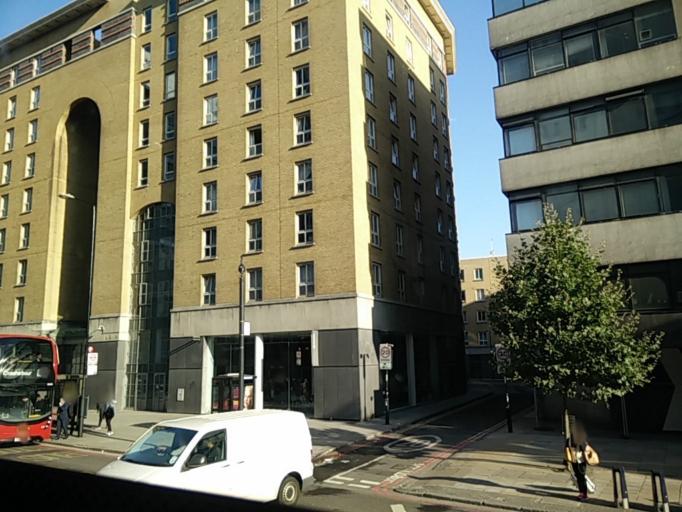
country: GB
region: England
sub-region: Greater London
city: Bethnal Green
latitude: 51.5149
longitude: -0.0663
